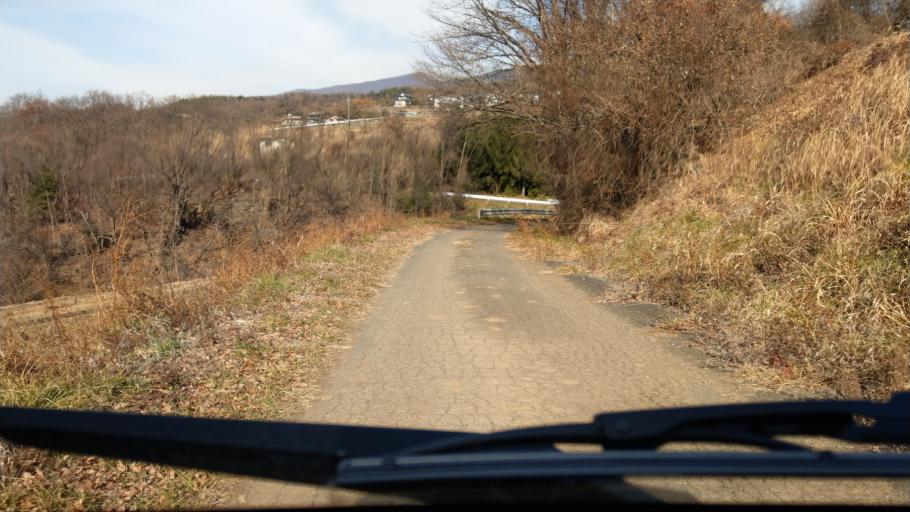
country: JP
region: Nagano
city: Komoro
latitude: 36.3480
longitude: 138.4179
